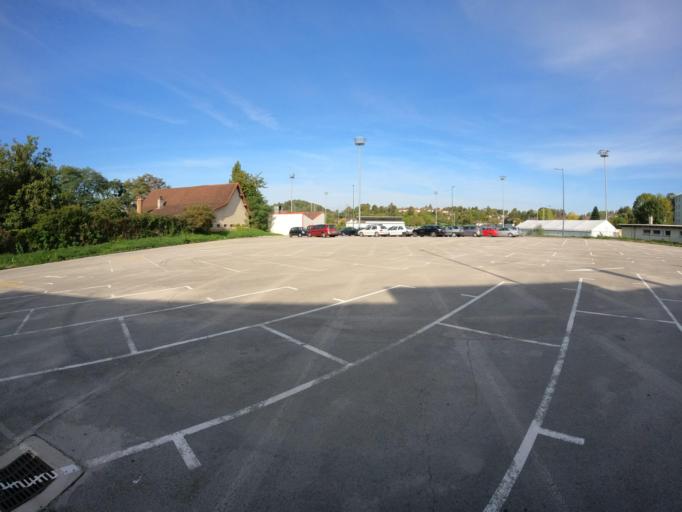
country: FR
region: Franche-Comte
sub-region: Departement du Jura
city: Lons-le-Saunier
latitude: 46.6761
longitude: 5.5419
